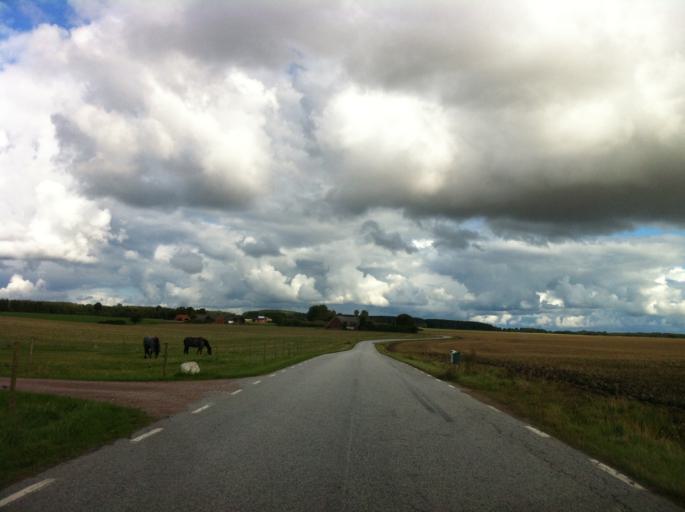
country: SE
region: Skane
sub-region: Eslovs Kommun
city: Eslov
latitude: 55.8783
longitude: 13.2599
